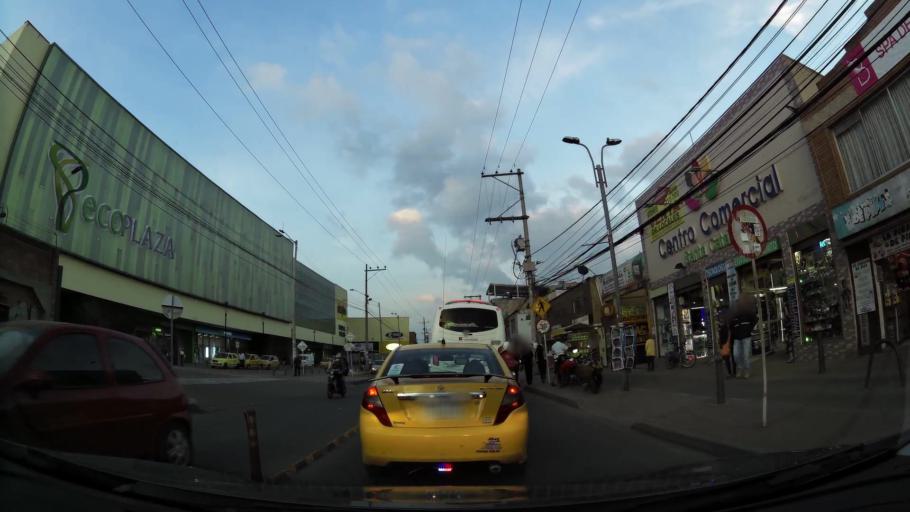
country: CO
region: Cundinamarca
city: Mosquera
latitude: 4.7120
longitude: -74.2219
